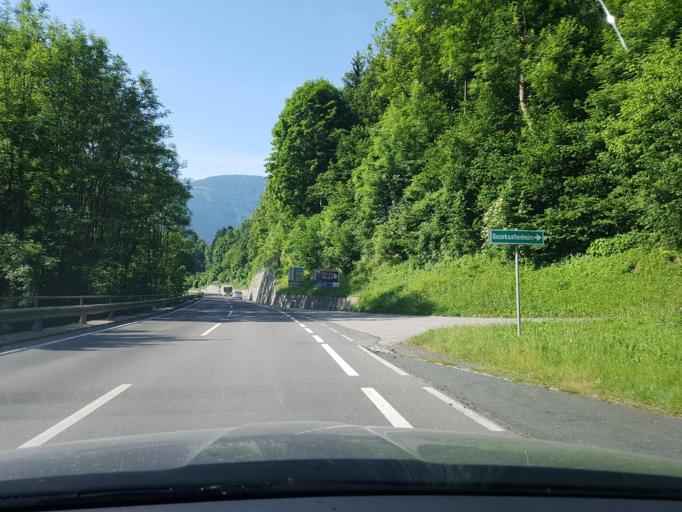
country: AT
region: Carinthia
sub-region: Politischer Bezirk Spittal an der Drau
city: Spittal an der Drau
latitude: 46.8060
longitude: 13.4959
